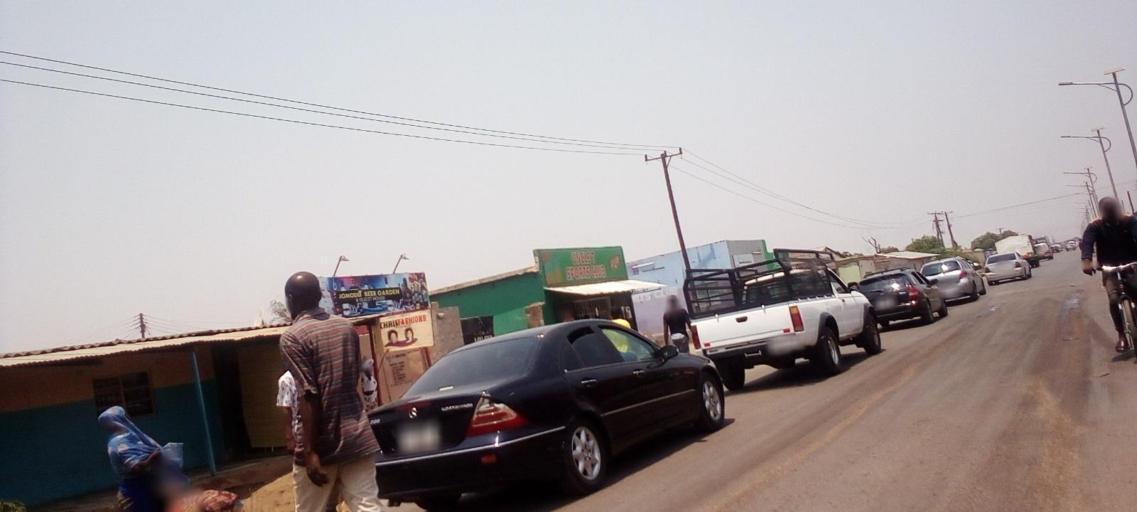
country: ZM
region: Lusaka
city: Lusaka
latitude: -15.4402
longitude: 28.2534
